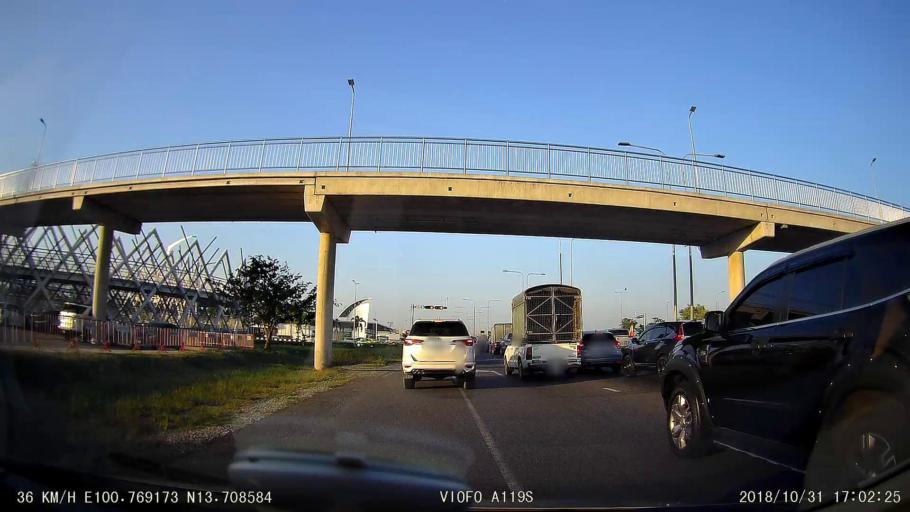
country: TH
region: Bangkok
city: Lat Krabang
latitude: 13.7087
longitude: 100.7692
